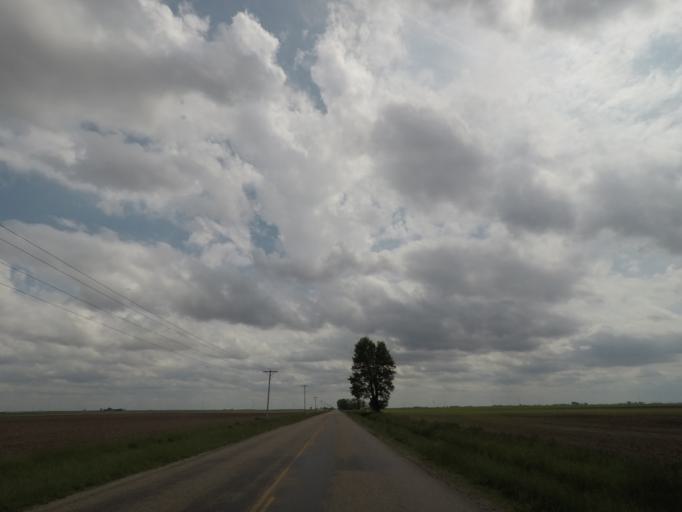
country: US
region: Illinois
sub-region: De Witt County
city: Clinton
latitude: 40.0921
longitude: -89.0859
